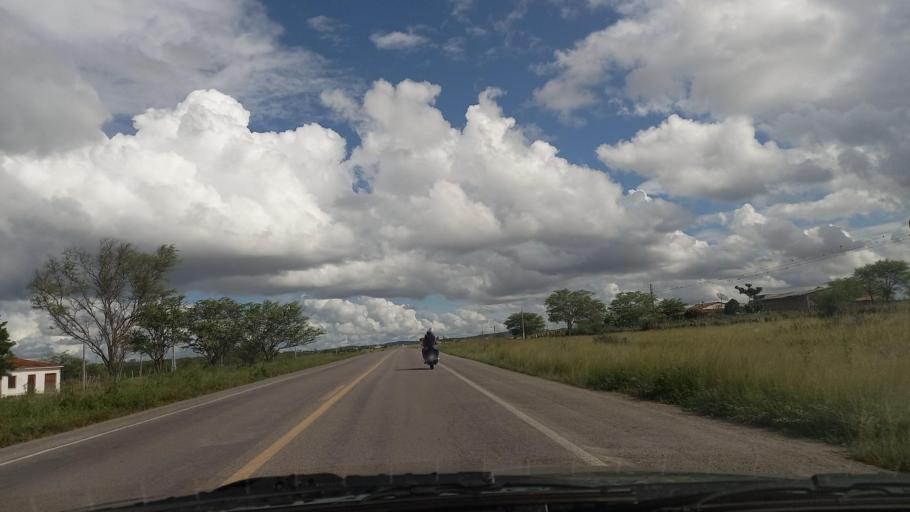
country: BR
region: Pernambuco
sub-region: Lajedo
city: Lajedo
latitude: -8.6174
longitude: -36.2994
